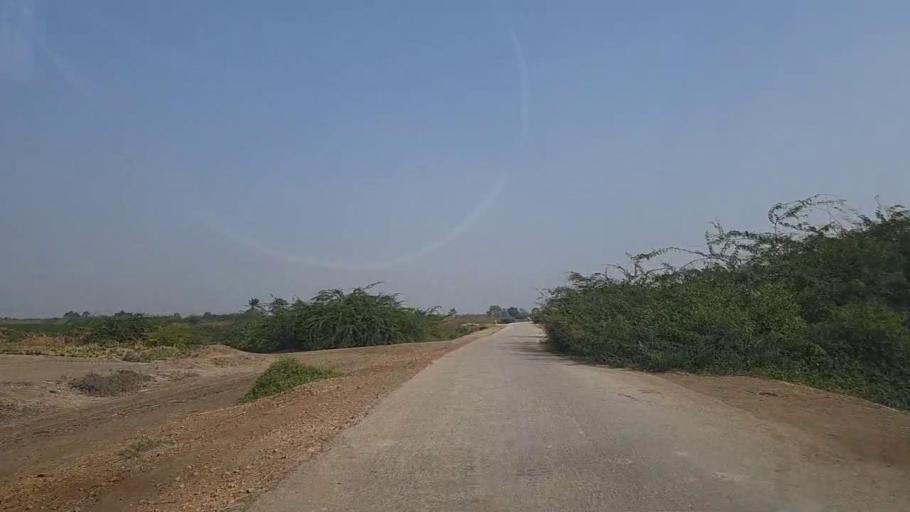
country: PK
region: Sindh
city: Keti Bandar
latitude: 24.2433
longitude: 67.7028
